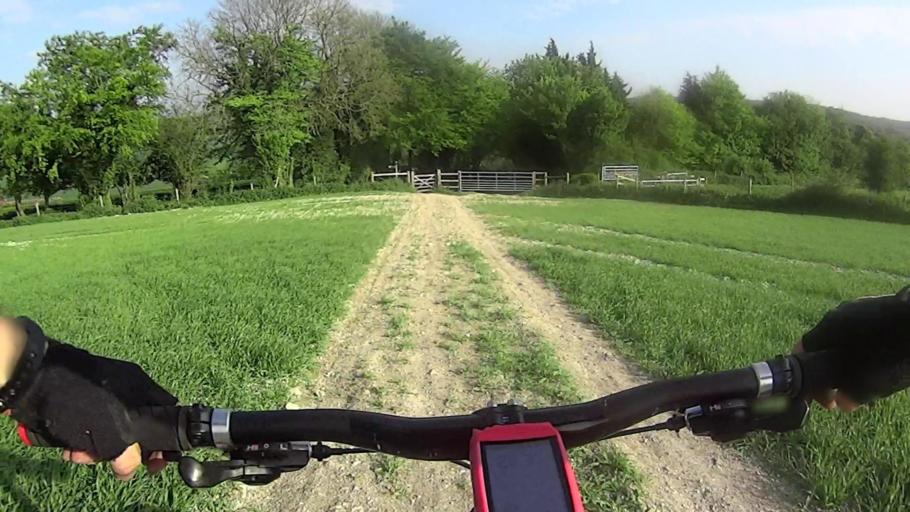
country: GB
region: England
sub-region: West Sussex
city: Fontwell
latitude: 50.9238
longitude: -0.6502
